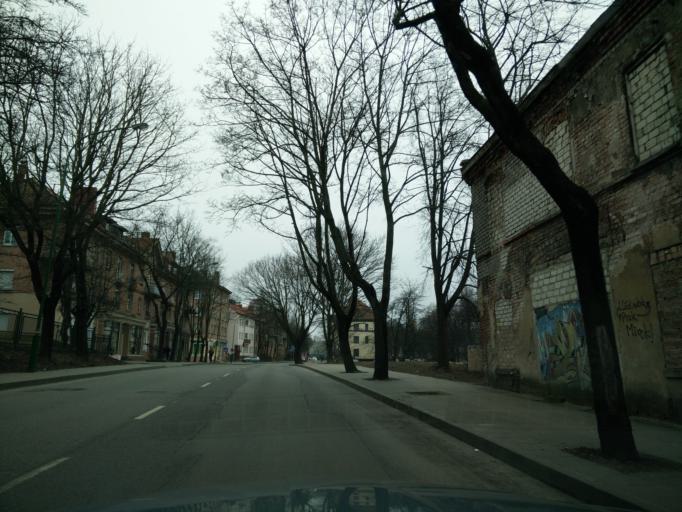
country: LT
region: Klaipedos apskritis
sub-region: Klaipeda
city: Klaipeda
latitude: 55.7059
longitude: 21.1382
